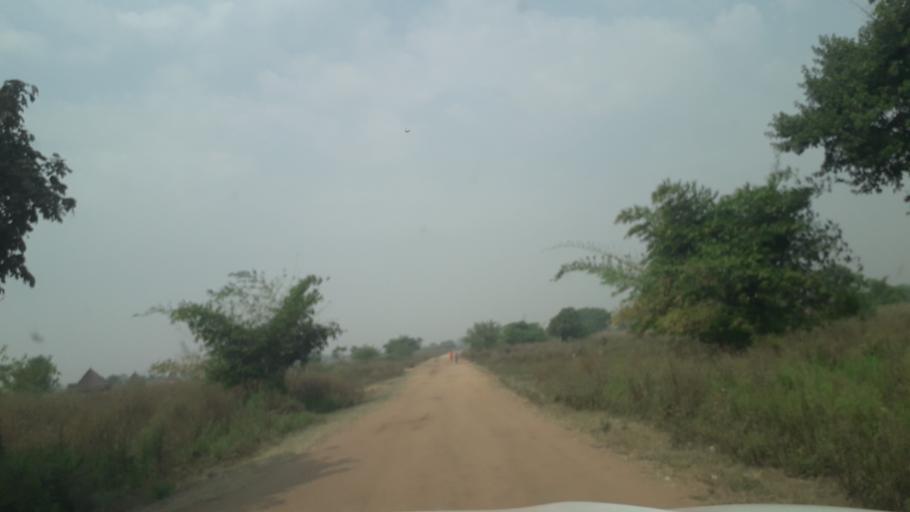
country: ET
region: Gambela
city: Gambela
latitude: 8.3288
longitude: 33.7334
